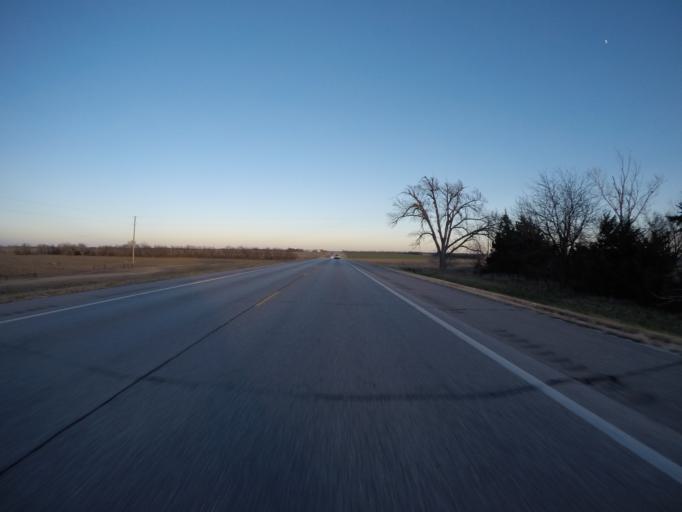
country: US
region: Kansas
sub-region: Marion County
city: Peabody
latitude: 38.1747
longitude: -97.1614
